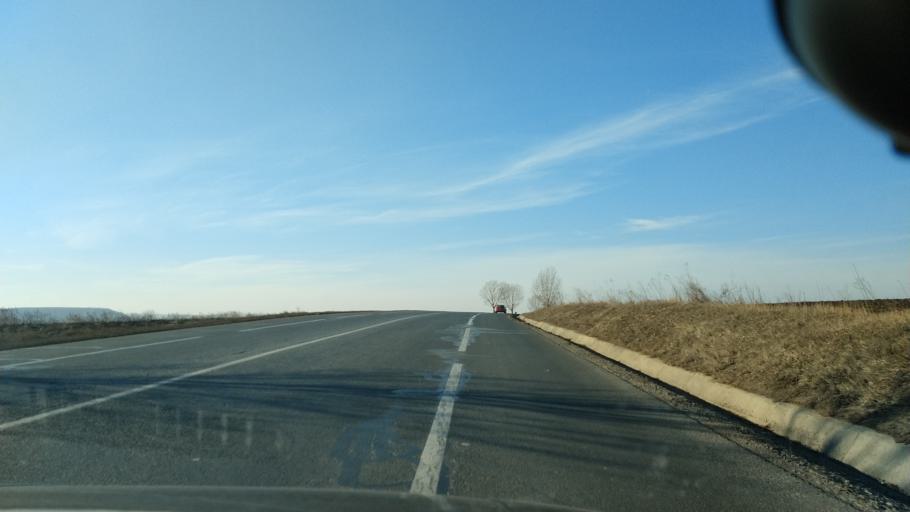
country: RO
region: Iasi
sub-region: Comuna Ion Neculce
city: Razboieni
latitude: 47.2205
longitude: 27.0975
